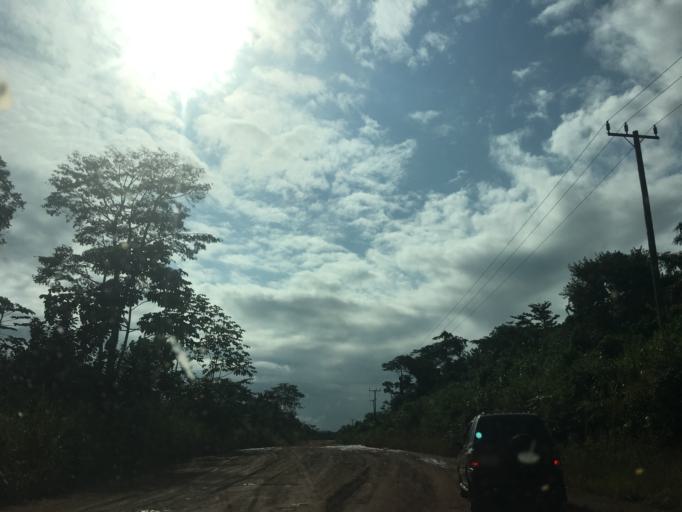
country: GH
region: Western
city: Wassa-Akropong
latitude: 5.9313
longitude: -2.4177
